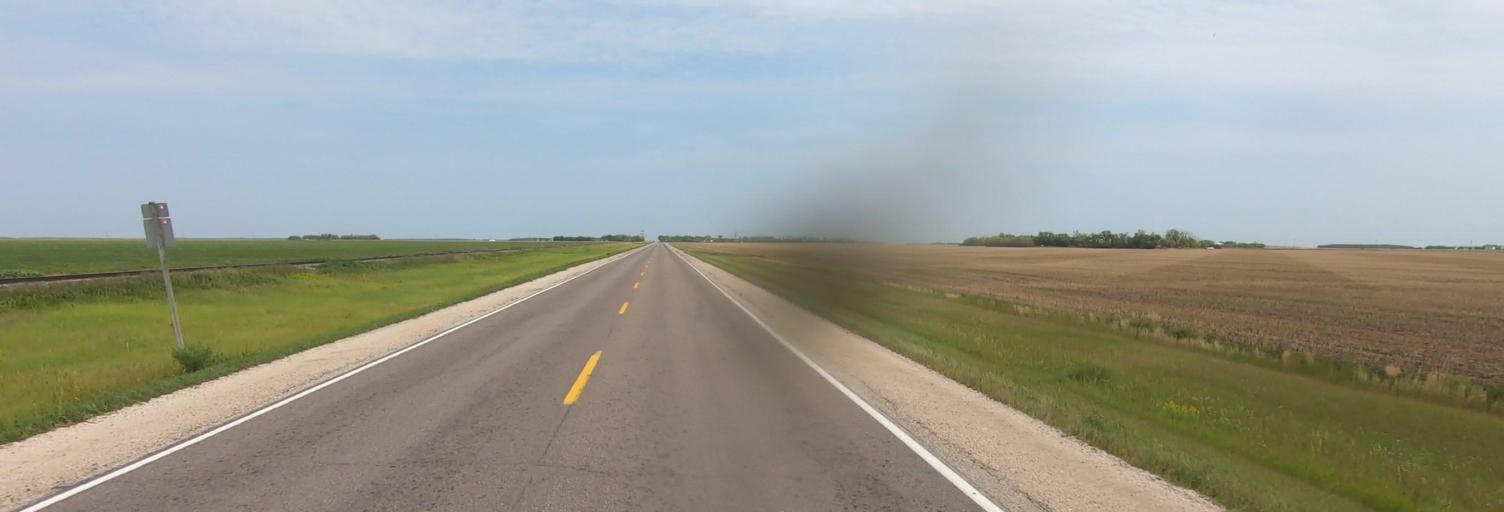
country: CA
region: Manitoba
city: Morris
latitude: 49.5943
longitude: -97.3355
